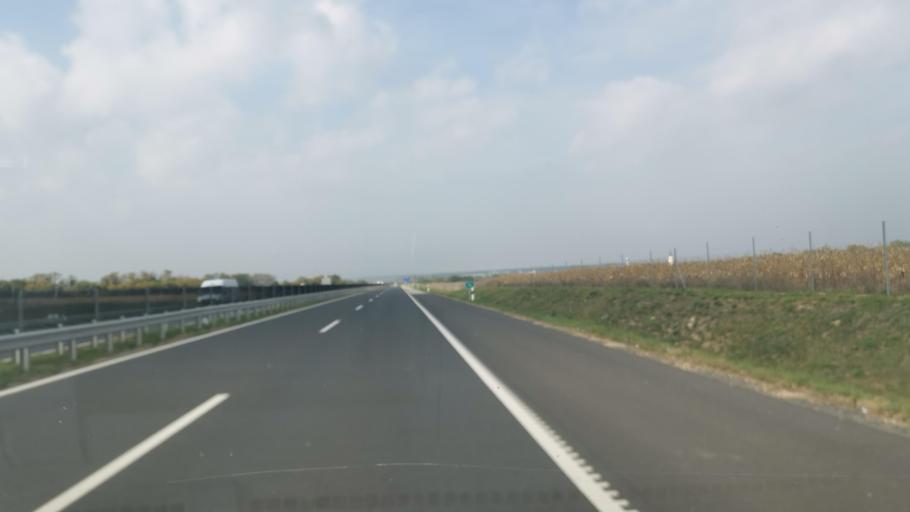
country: HU
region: Gyor-Moson-Sopron
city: Nagycenk
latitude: 47.5923
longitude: 16.7054
